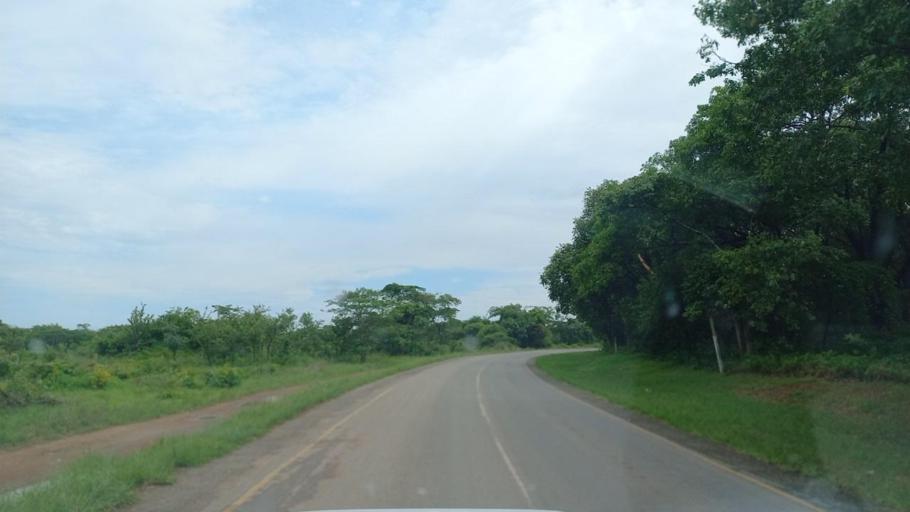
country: ZM
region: Copperbelt
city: Kitwe
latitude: -12.8875
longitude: 28.3110
